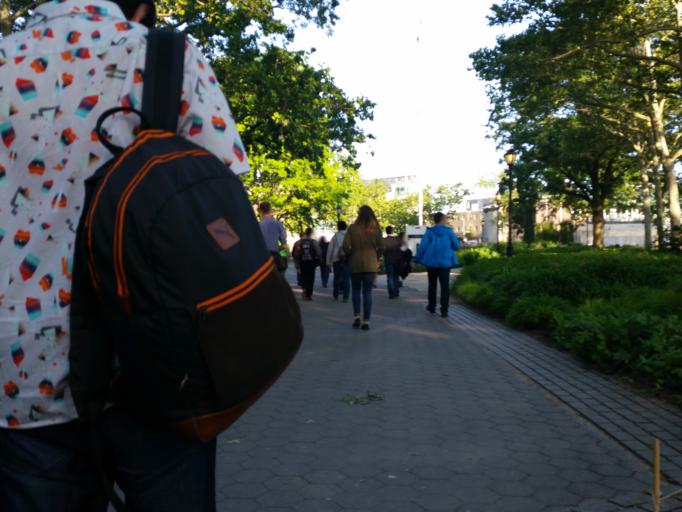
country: US
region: New York
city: New York City
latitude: 40.7024
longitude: -74.0158
